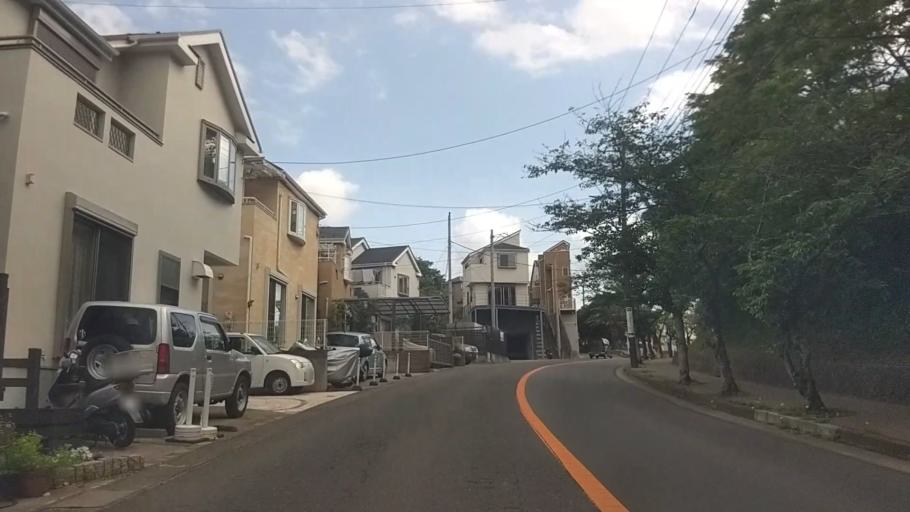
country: JP
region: Kanagawa
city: Zushi
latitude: 35.3068
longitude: 139.5718
